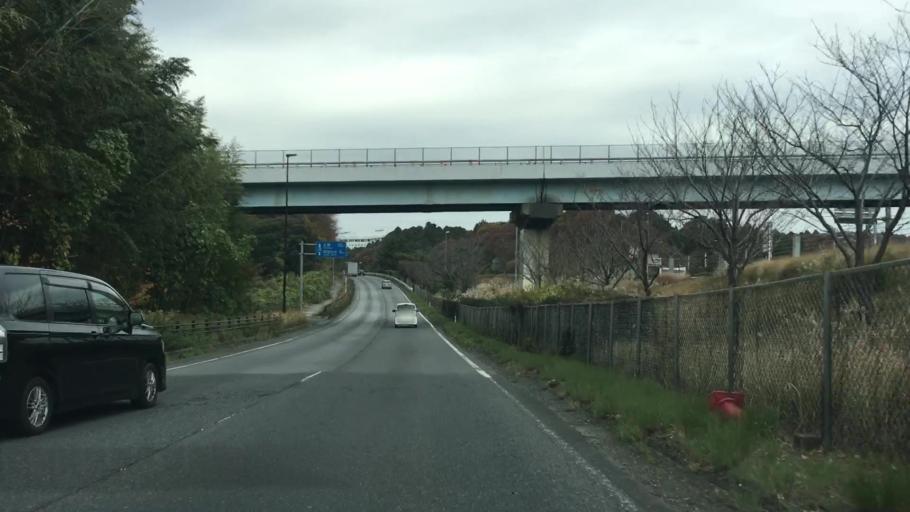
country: JP
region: Chiba
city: Narita
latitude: 35.7814
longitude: 140.3774
